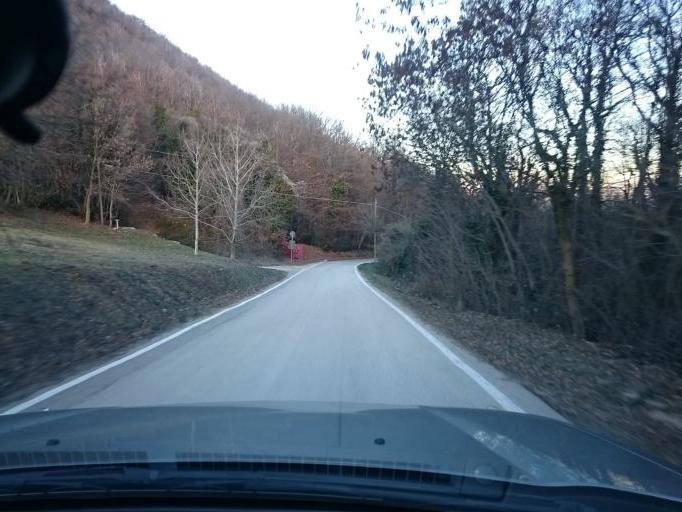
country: IT
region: Veneto
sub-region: Provincia di Padova
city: Bastia
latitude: 45.3572
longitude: 11.6667
